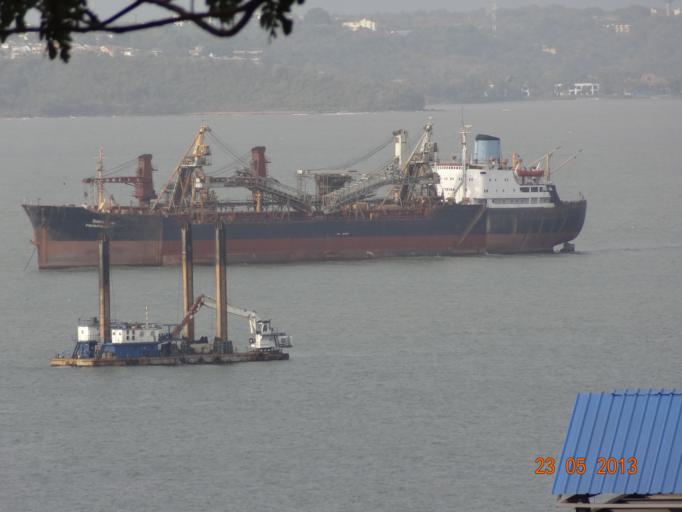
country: IN
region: Goa
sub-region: South Goa
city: Marmagao
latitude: 15.4105
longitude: 73.7961
